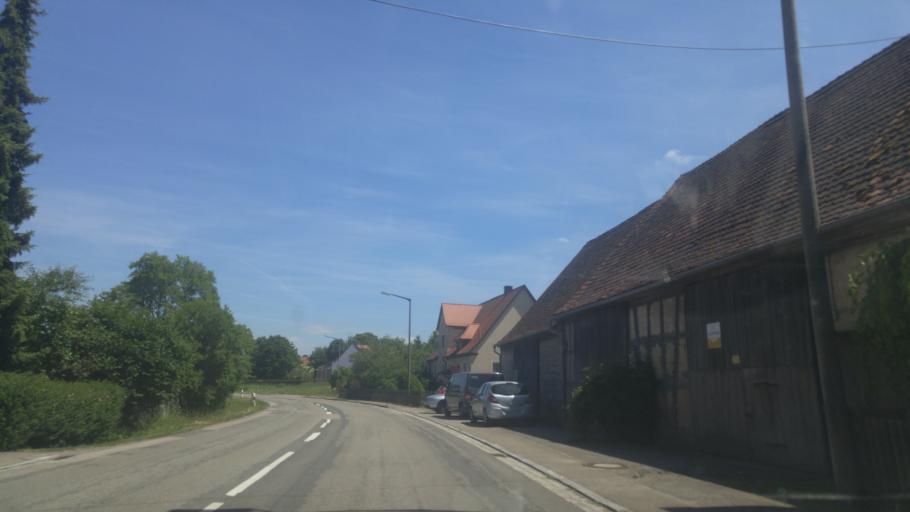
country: DE
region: Bavaria
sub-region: Regierungsbezirk Mittelfranken
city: Gallmersgarten
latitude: 49.4452
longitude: 10.2417
